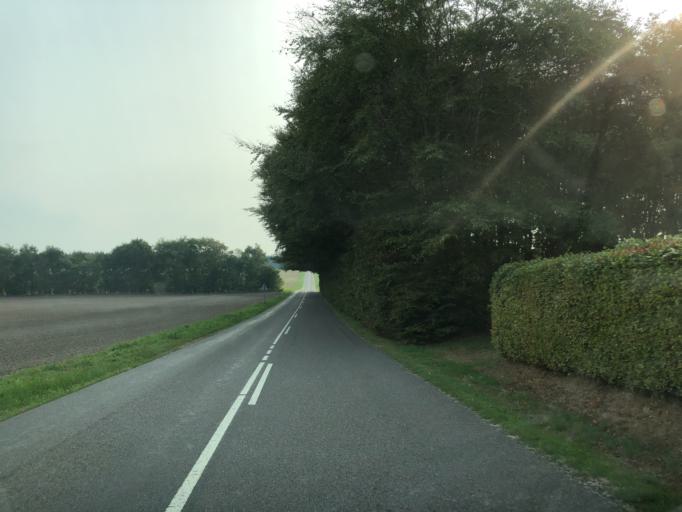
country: DK
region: Central Jutland
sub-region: Ringkobing-Skjern Kommune
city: Videbaek
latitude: 56.0701
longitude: 8.6971
